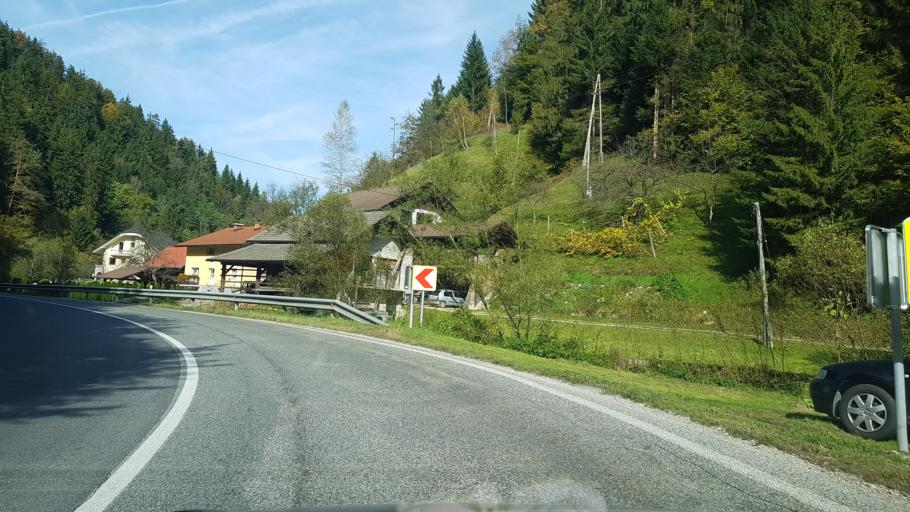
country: SI
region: Dobrna
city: Dobrna
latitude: 46.4036
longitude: 15.1799
